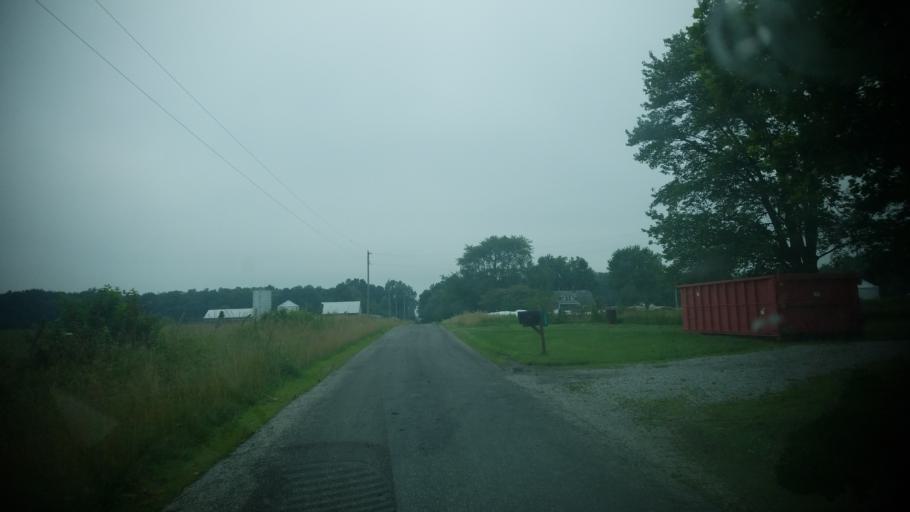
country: US
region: Illinois
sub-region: Clay County
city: Flora
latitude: 38.5735
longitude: -88.3835
